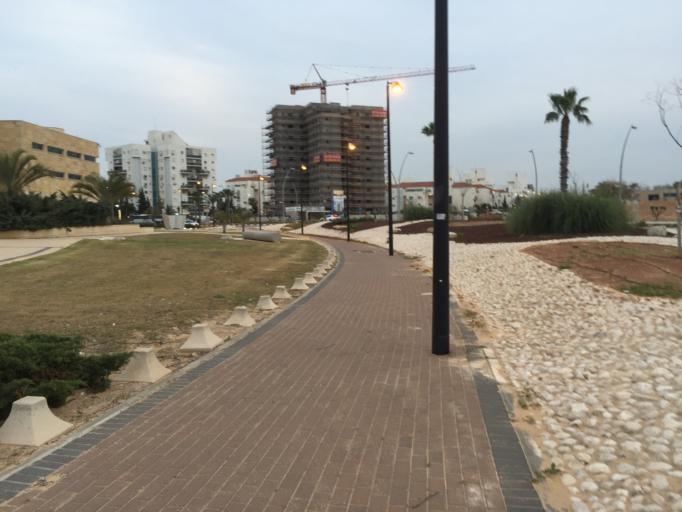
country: IL
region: Haifa
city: Qesarya
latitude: 32.5039
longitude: 34.9200
